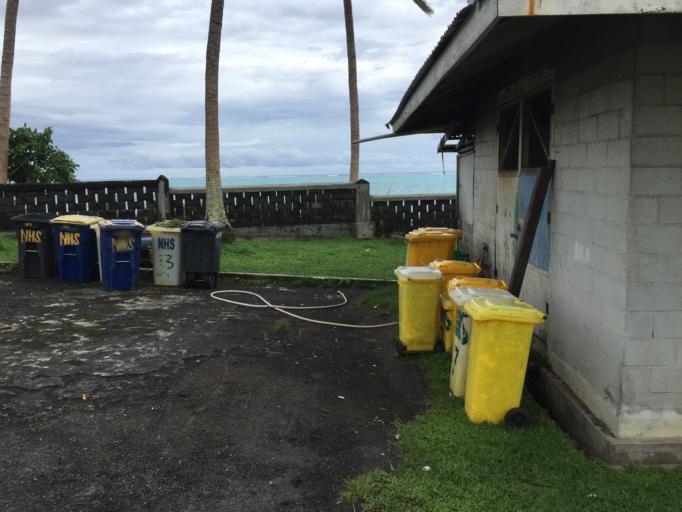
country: WS
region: Fa`asaleleaga
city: Safotulafai
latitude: -13.6661
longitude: -172.1776
